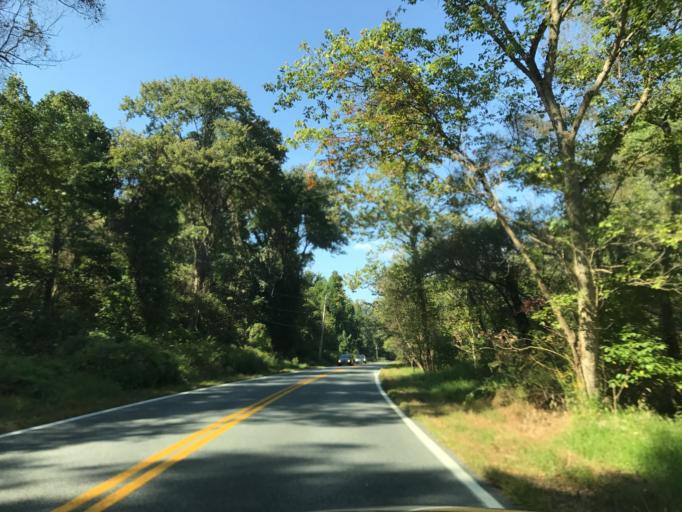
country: US
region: Maryland
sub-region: Harford County
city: Havre de Grace
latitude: 39.6320
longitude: -76.1463
